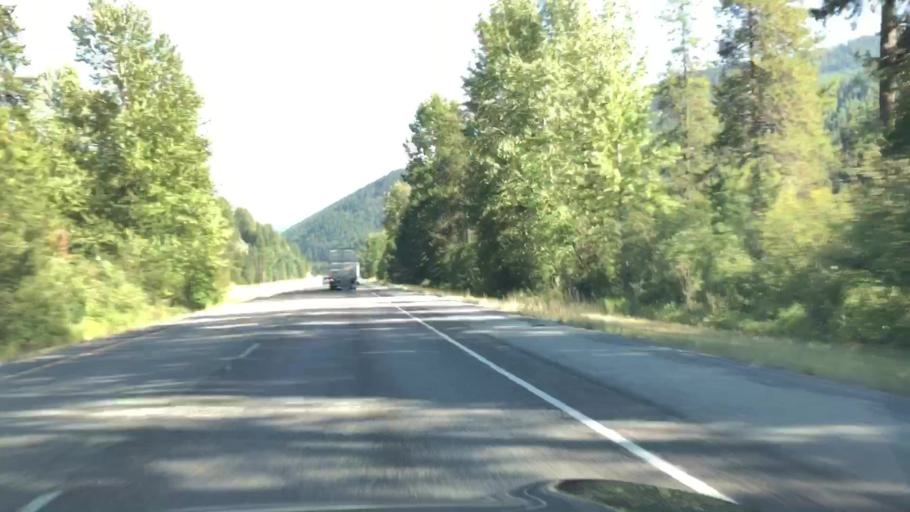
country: US
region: Montana
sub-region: Sanders County
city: Thompson Falls
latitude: 47.3660
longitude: -115.3302
